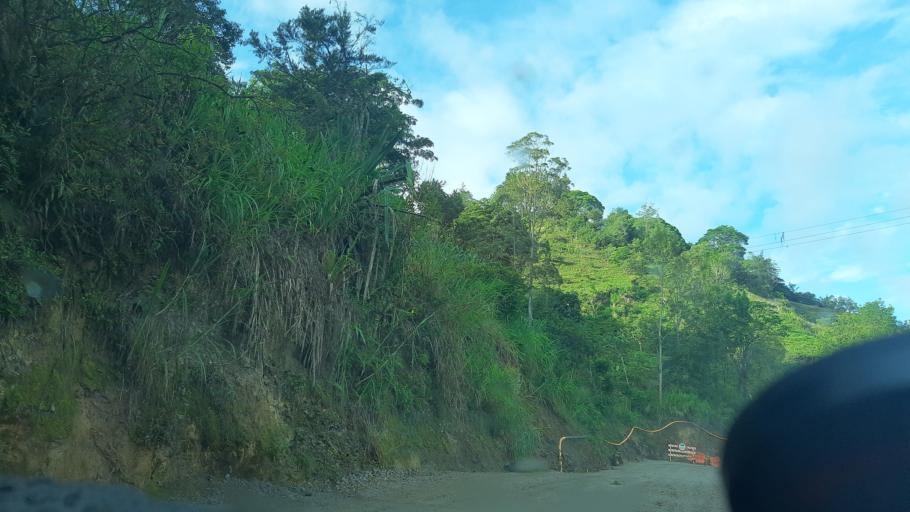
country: CO
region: Cundinamarca
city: Tenza
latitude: 5.0761
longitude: -73.3973
